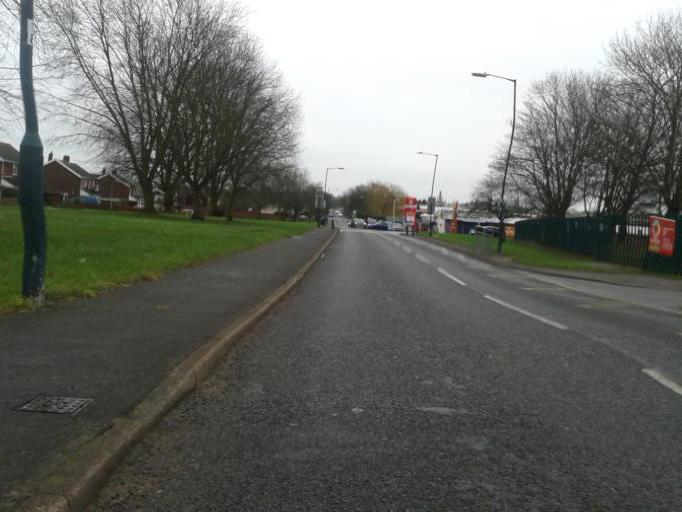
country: GB
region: England
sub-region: Warwickshire
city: Atherstone
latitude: 52.5801
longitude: -1.5395
